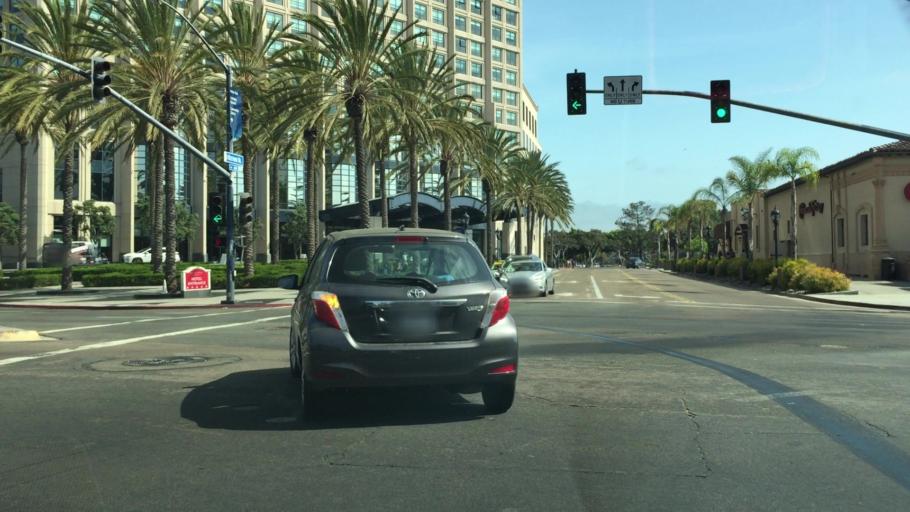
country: US
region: California
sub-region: San Diego County
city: San Diego
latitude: 32.7115
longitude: -117.1691
